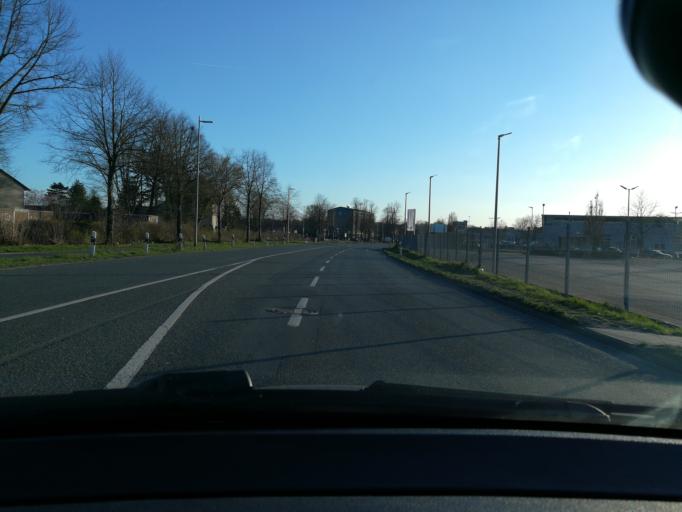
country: DE
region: North Rhine-Westphalia
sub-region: Regierungsbezirk Detmold
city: Oerlinghausen
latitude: 51.9530
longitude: 8.5767
